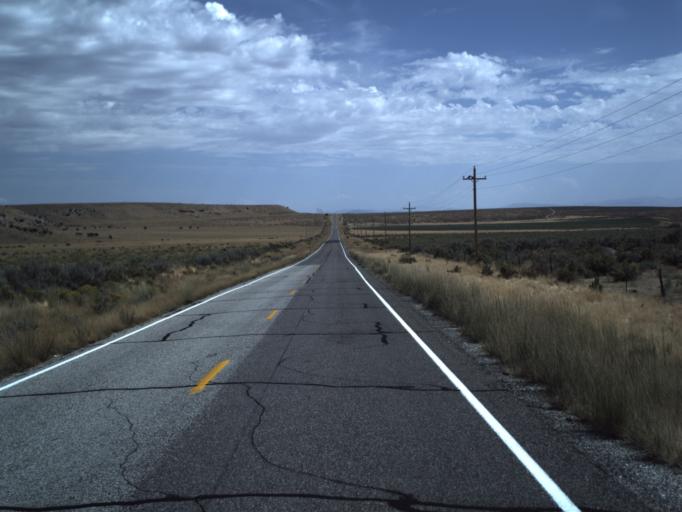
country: US
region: Idaho
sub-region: Cassia County
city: Burley
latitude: 41.8167
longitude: -113.2417
